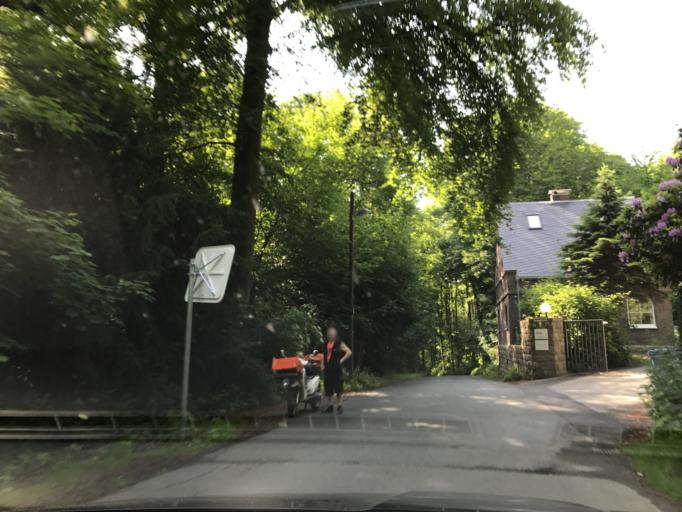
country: DE
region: North Rhine-Westphalia
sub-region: Regierungsbezirk Dusseldorf
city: Essen
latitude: 51.4161
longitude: 7.0100
